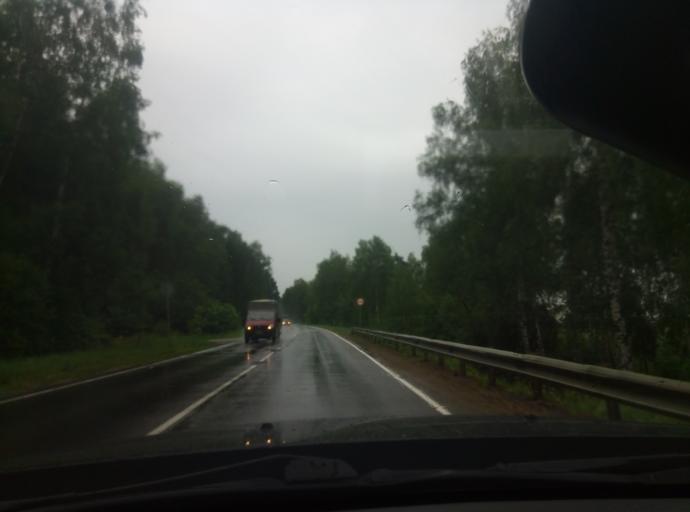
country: RU
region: Kaluga
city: Vysokinichi
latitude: 54.9014
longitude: 37.0104
